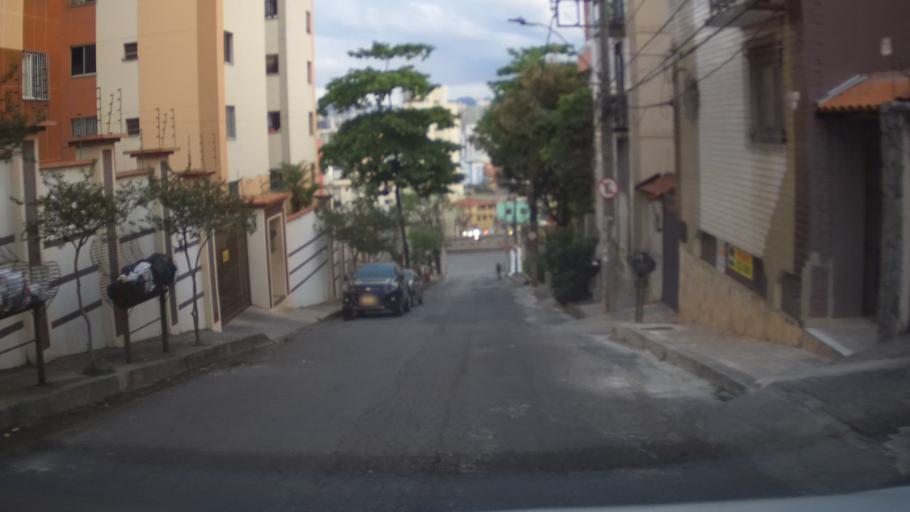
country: BR
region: Minas Gerais
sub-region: Belo Horizonte
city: Belo Horizonte
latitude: -19.9021
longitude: -43.9295
